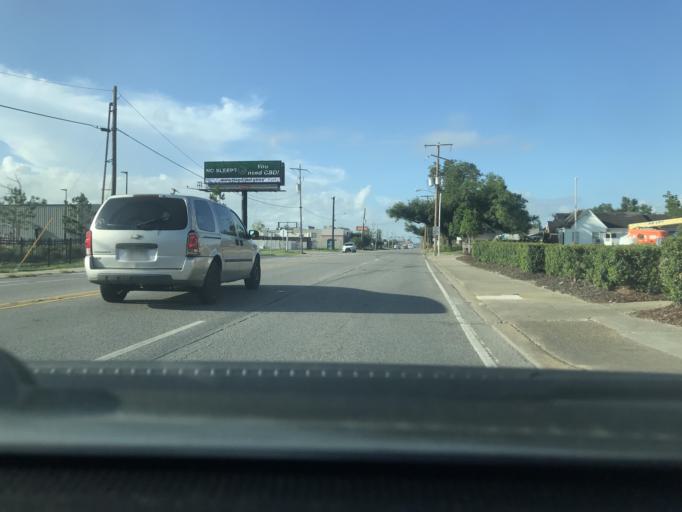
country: US
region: Louisiana
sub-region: Calcasieu Parish
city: Lake Charles
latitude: 30.2126
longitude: -93.2188
